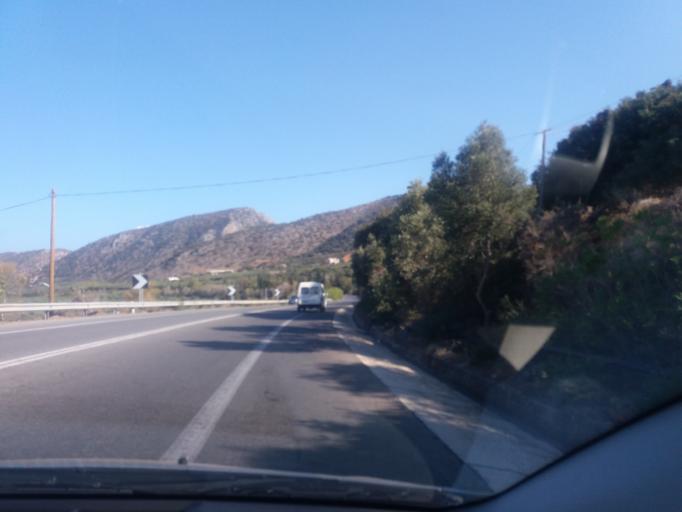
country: GR
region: Crete
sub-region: Nomos Lasithiou
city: Sision
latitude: 35.2931
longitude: 25.5189
